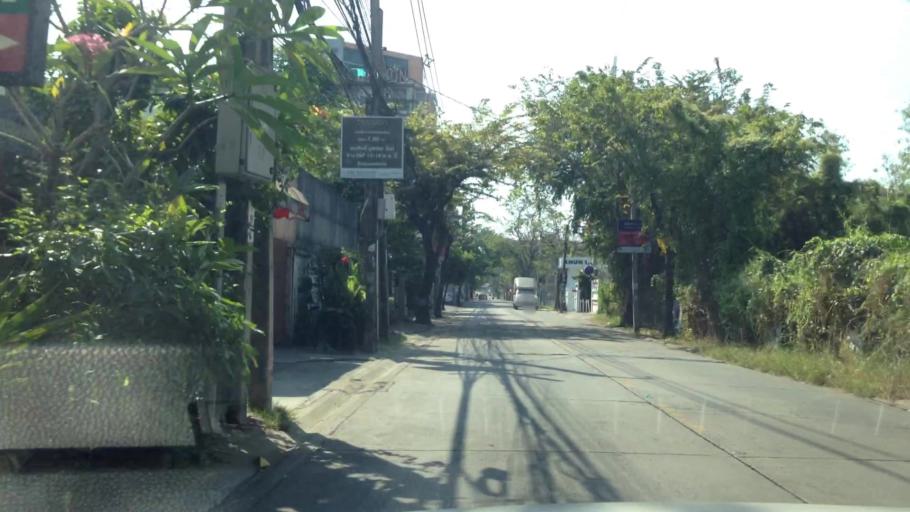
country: TH
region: Bangkok
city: Bang Kapi
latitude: 13.7676
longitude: 100.6328
